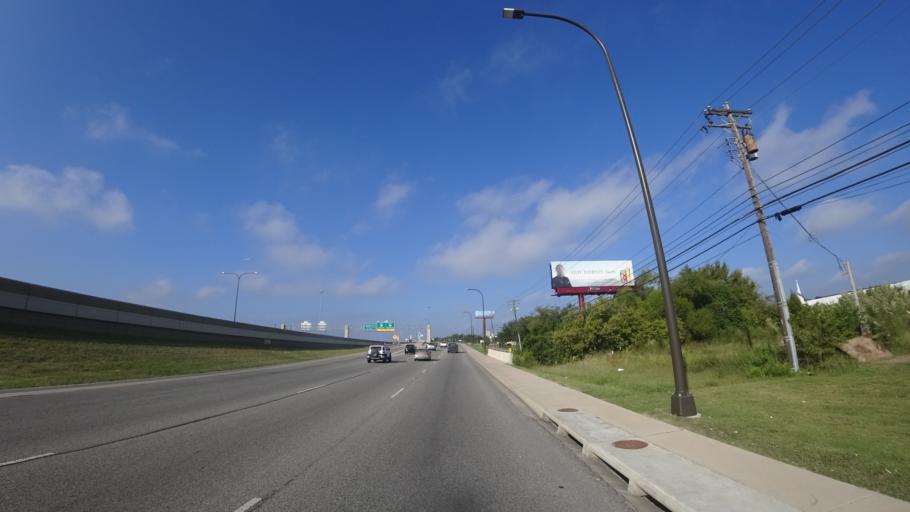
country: US
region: Texas
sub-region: Travis County
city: Austin
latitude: 30.3286
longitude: -97.6614
